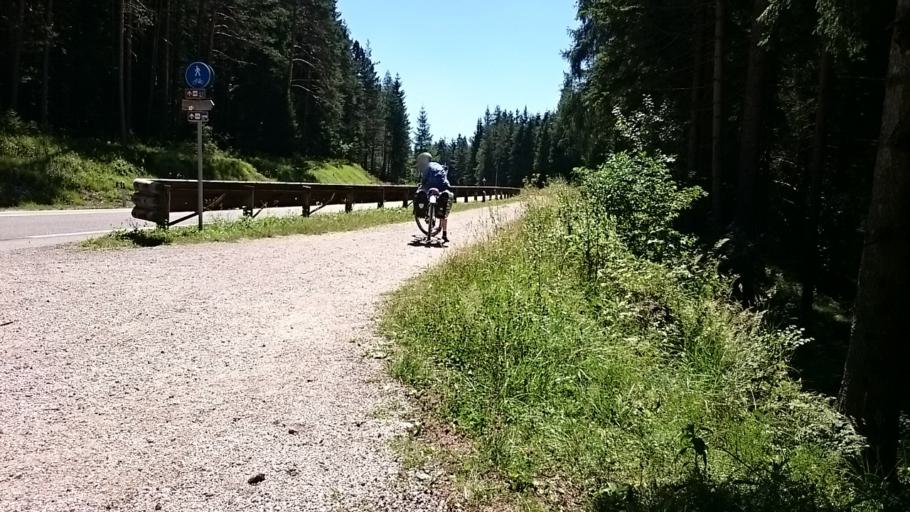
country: IT
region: Veneto
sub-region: Provincia di Belluno
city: San Vito
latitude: 46.4938
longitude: 12.1798
